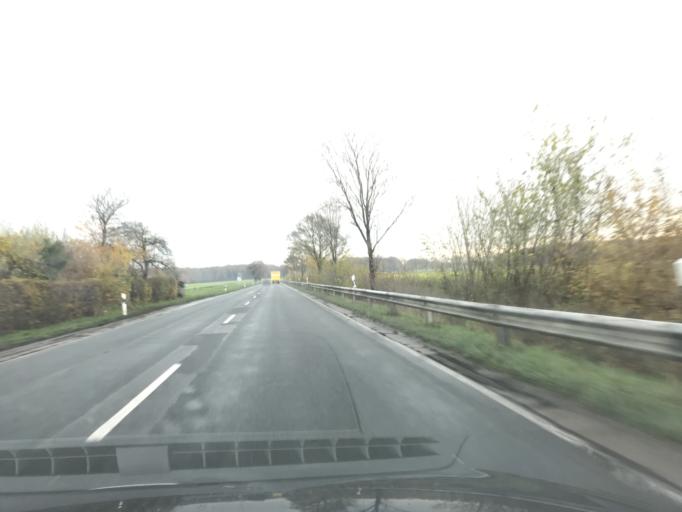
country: DE
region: North Rhine-Westphalia
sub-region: Regierungsbezirk Munster
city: Everswinkel
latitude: 51.9284
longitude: 7.8731
